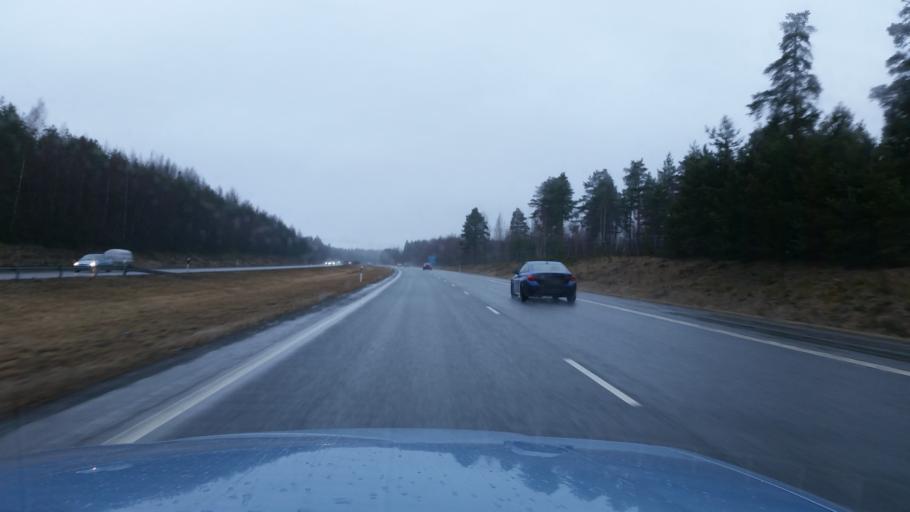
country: FI
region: Haeme
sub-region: Haemeenlinna
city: Parola
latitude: 61.0364
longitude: 24.3826
